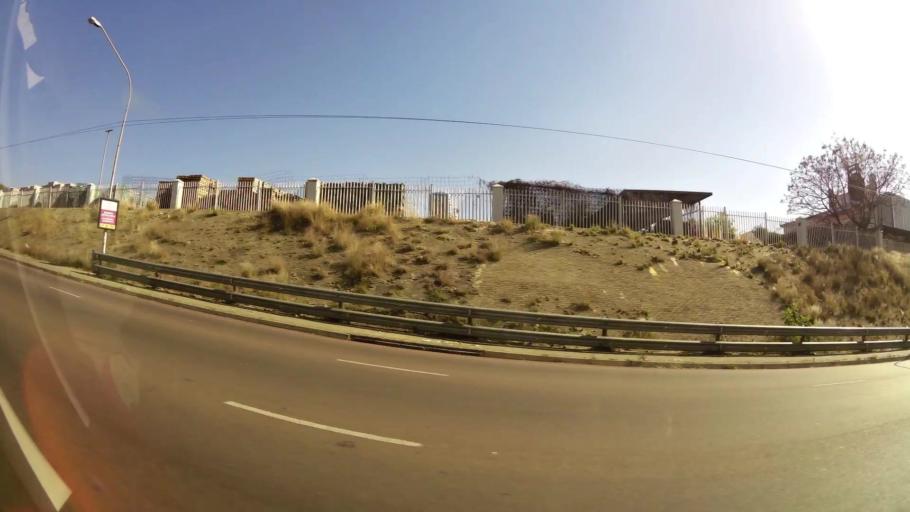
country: ZA
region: Gauteng
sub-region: City of Tshwane Metropolitan Municipality
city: Pretoria
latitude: -25.7234
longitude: 28.2049
